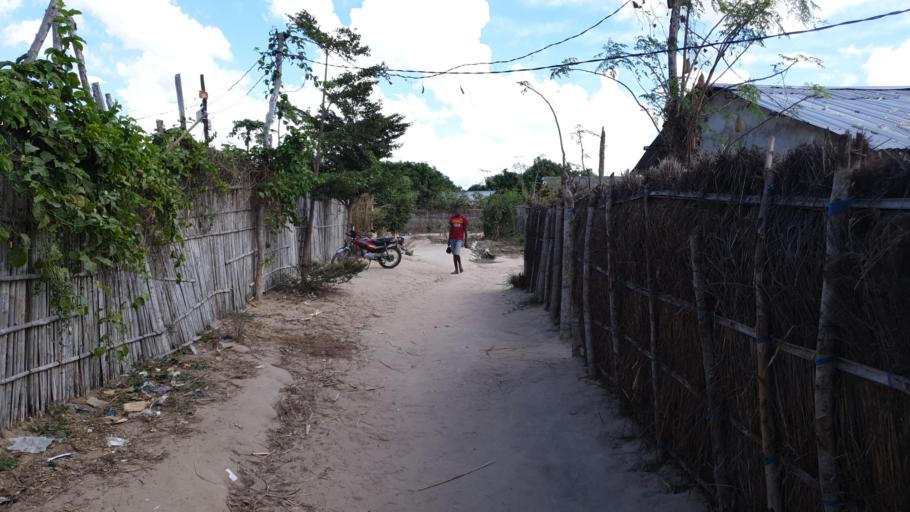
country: MZ
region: Nampula
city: Nacala
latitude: -14.5781
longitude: 40.7024
